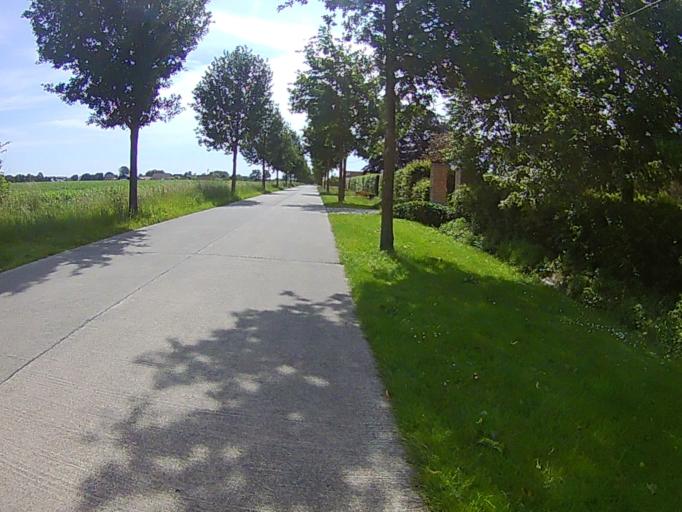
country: BE
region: Flanders
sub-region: Provincie Antwerpen
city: Lier
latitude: 51.0924
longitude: 4.5900
